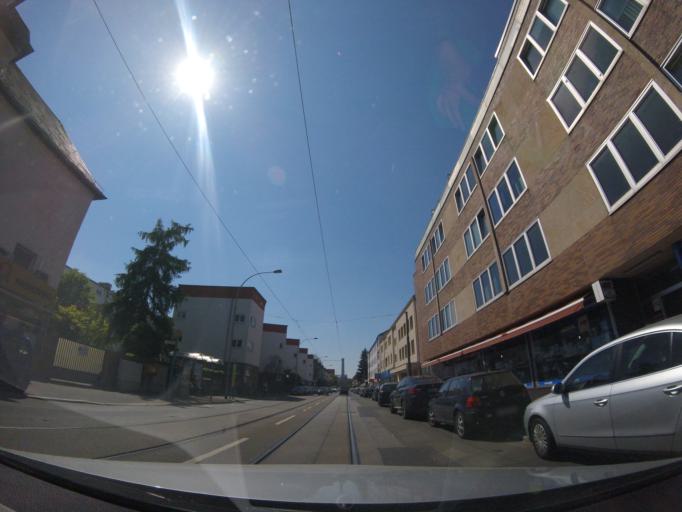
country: DE
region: Hesse
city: Niederrad
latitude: 50.0865
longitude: 8.6420
